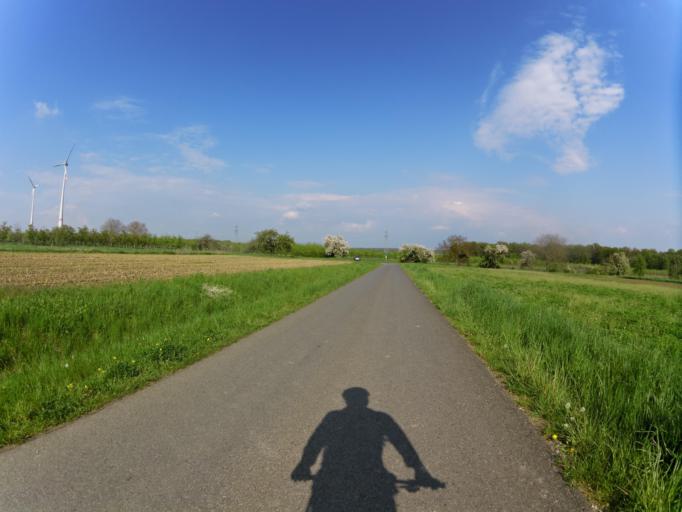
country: DE
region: Bavaria
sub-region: Regierungsbezirk Unterfranken
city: Sommerhausen
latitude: 49.7089
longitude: 10.0506
